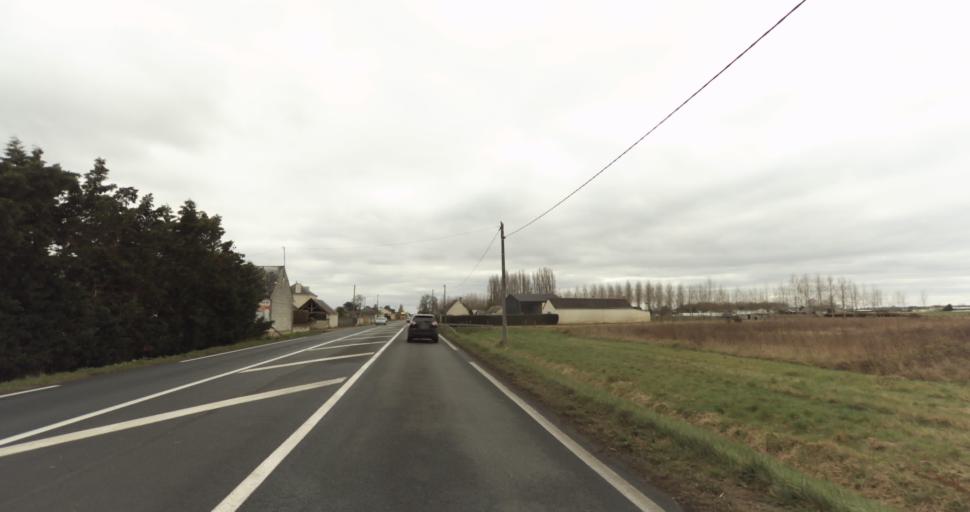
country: FR
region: Pays de la Loire
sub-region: Departement de Maine-et-Loire
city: Vivy
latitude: 47.3220
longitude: -0.0523
